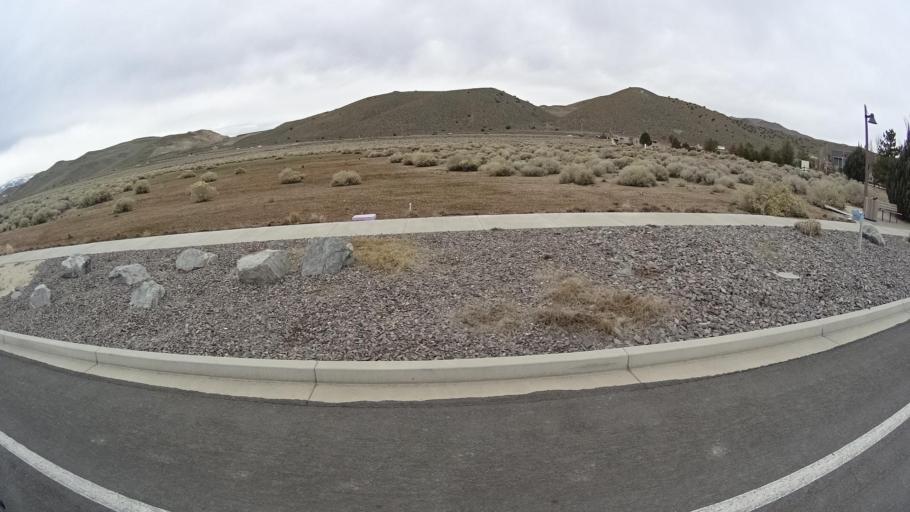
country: US
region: Nevada
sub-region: Washoe County
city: Spanish Springs
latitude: 39.6142
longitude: -119.7243
